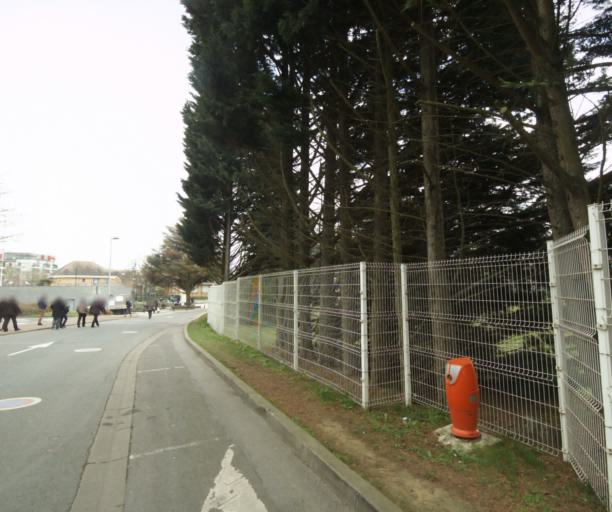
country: FR
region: Ile-de-France
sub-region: Departement du Val-d'Oise
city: Vaureal
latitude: 49.0520
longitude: 2.0351
